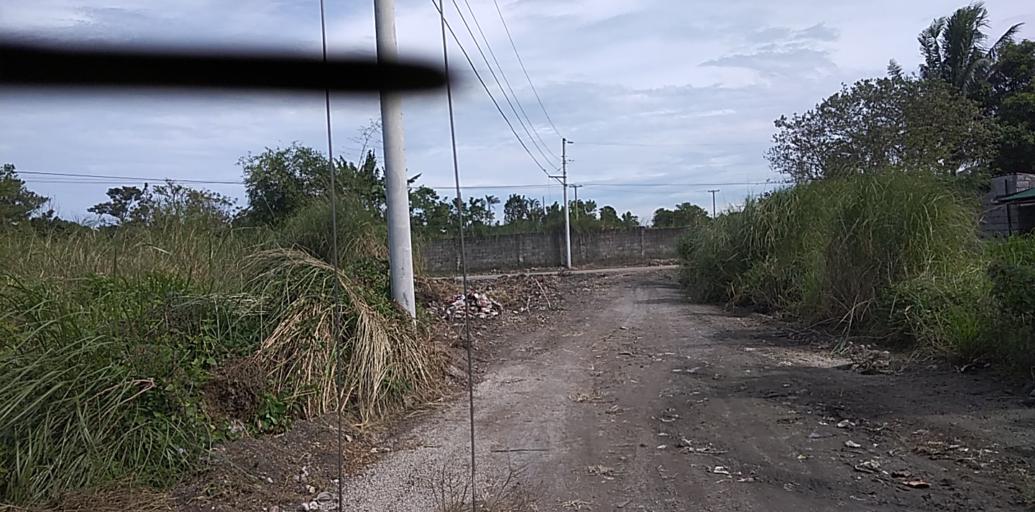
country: PH
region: Central Luzon
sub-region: Province of Pampanga
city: Angeles City
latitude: 15.1300
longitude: 120.5563
